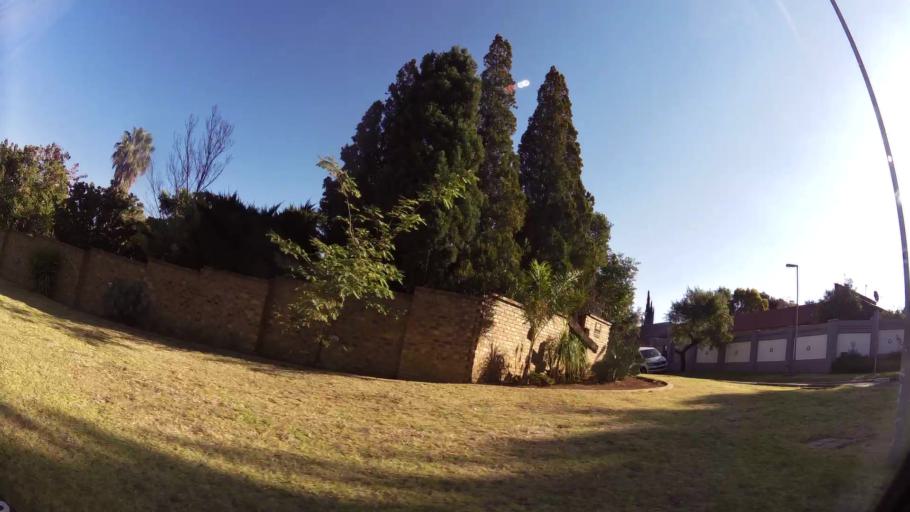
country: ZA
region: Gauteng
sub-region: City of Johannesburg Metropolitan Municipality
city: Johannesburg
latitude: -26.2990
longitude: 28.0611
